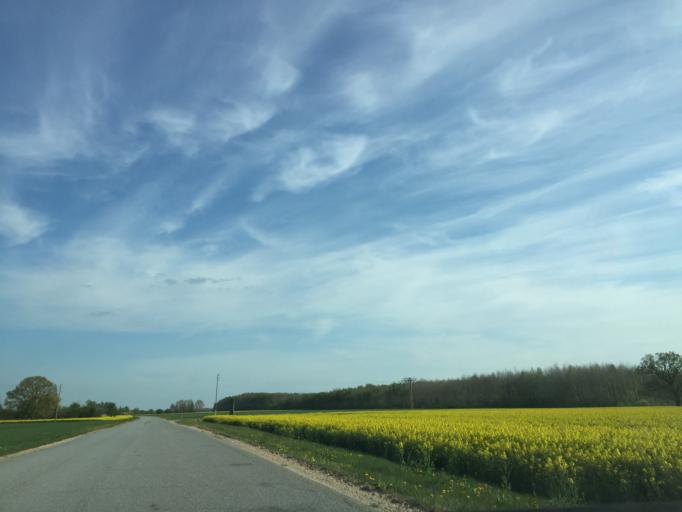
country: LV
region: Bauskas Rajons
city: Bauska
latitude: 56.3850
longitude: 24.2078
